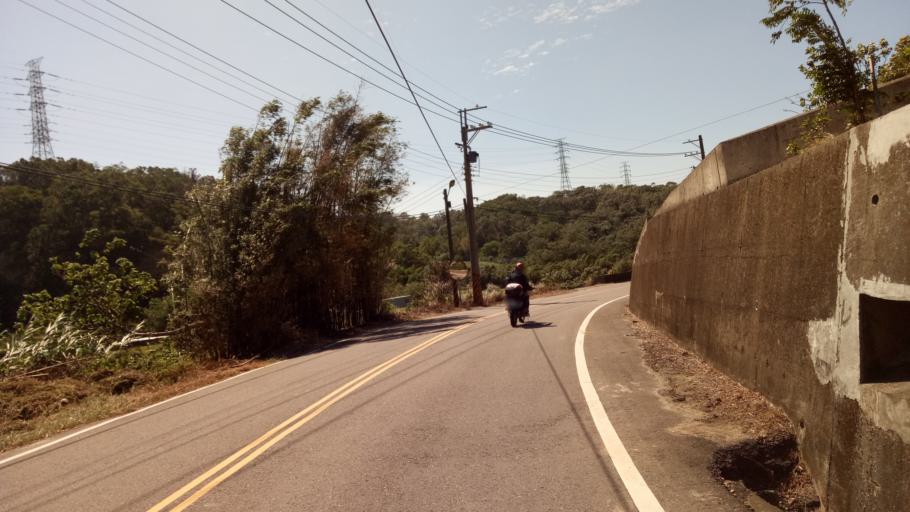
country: TW
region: Taiwan
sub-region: Hsinchu
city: Hsinchu
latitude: 24.7398
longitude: 120.9544
